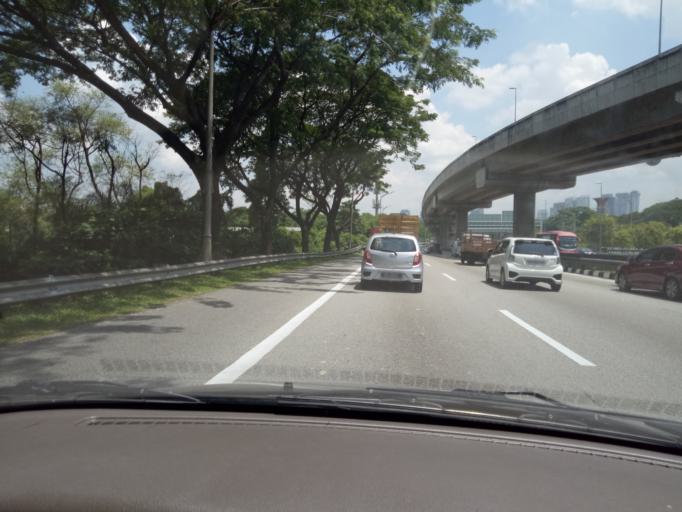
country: MY
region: Kuala Lumpur
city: Kuala Lumpur
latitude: 3.1222
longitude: 101.7065
